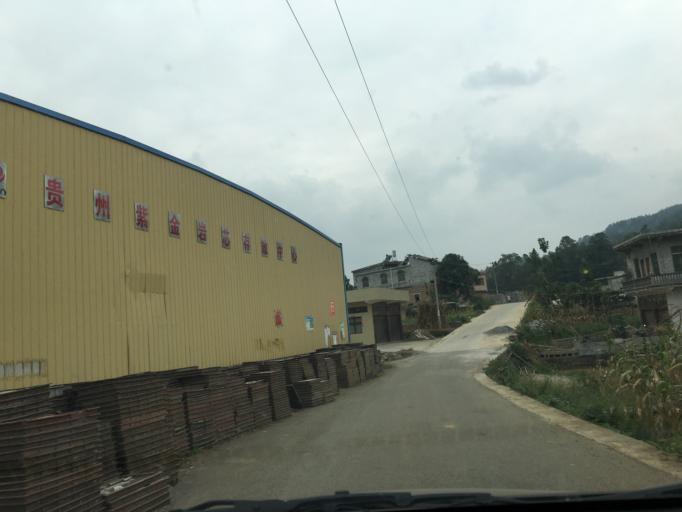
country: CN
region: Guangxi Zhuangzu Zizhiqu
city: Xinzhou
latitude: 25.5421
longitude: 105.5822
